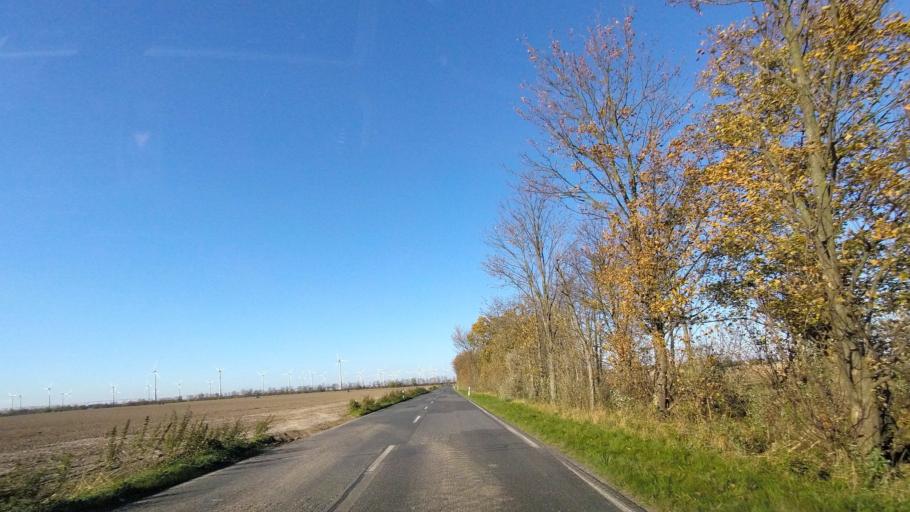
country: DE
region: Saxony-Anhalt
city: Zahna
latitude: 51.9817
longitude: 12.8587
